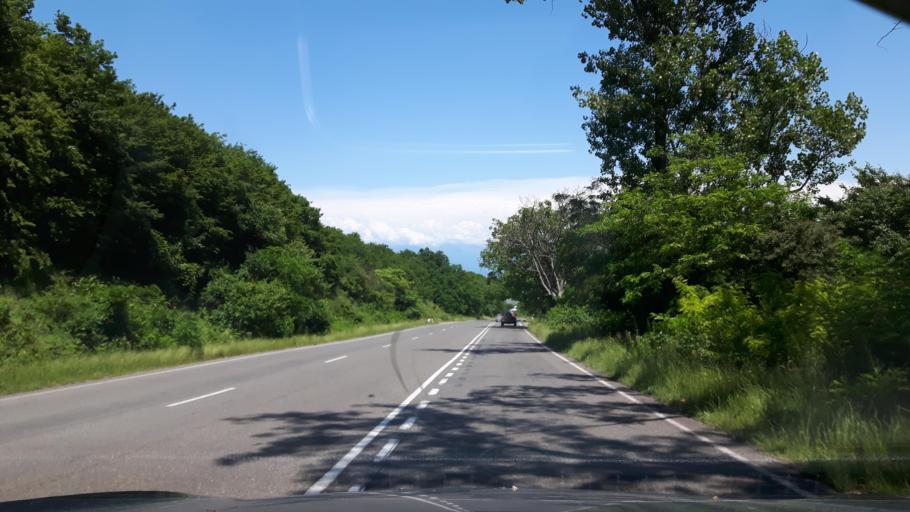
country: GE
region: Kakheti
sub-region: Gurjaani
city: Gurjaani
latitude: 41.6818
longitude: 45.8442
